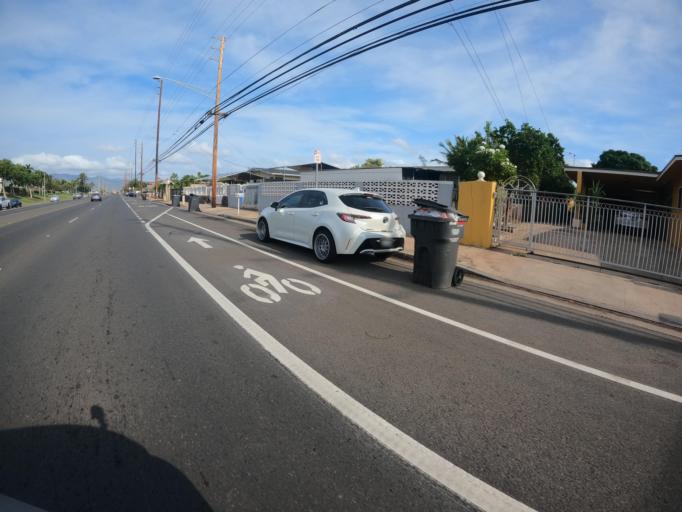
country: US
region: Hawaii
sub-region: Honolulu County
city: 'Ewa Beach
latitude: 21.3204
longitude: -158.0148
